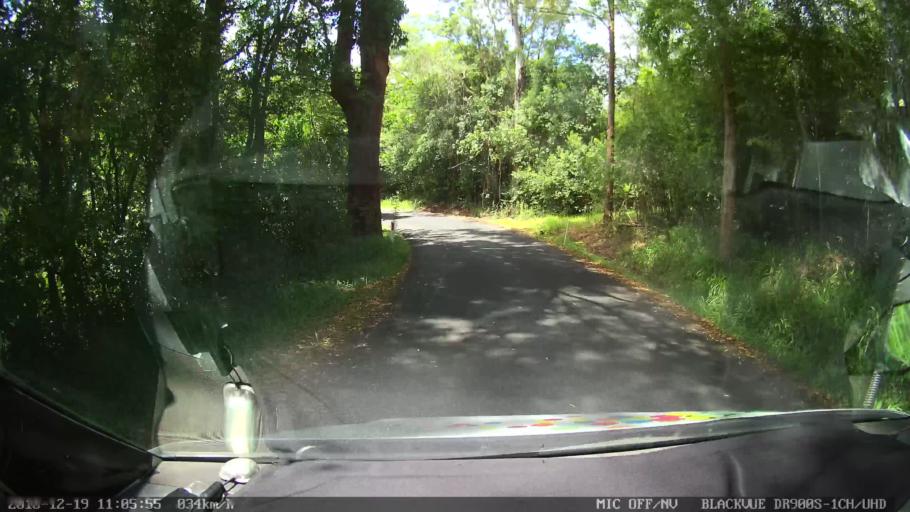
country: AU
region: New South Wales
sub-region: Lismore Municipality
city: Nimbin
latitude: -28.6200
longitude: 153.2653
